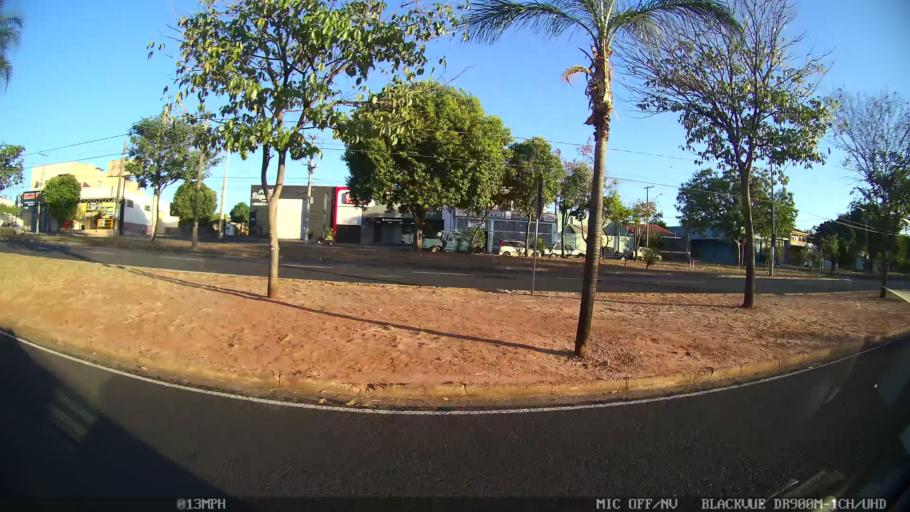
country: BR
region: Sao Paulo
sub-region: Sao Jose Do Rio Preto
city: Sao Jose do Rio Preto
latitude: -20.7796
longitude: -49.3704
